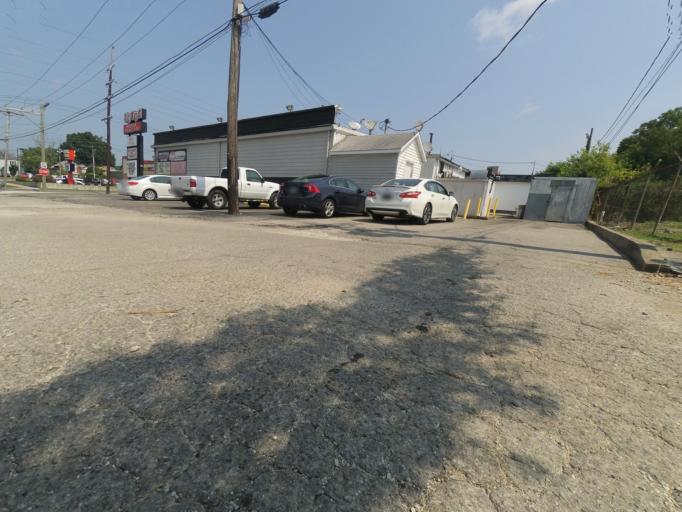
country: US
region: West Virginia
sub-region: Cabell County
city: Huntington
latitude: 38.4244
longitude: -82.4121
